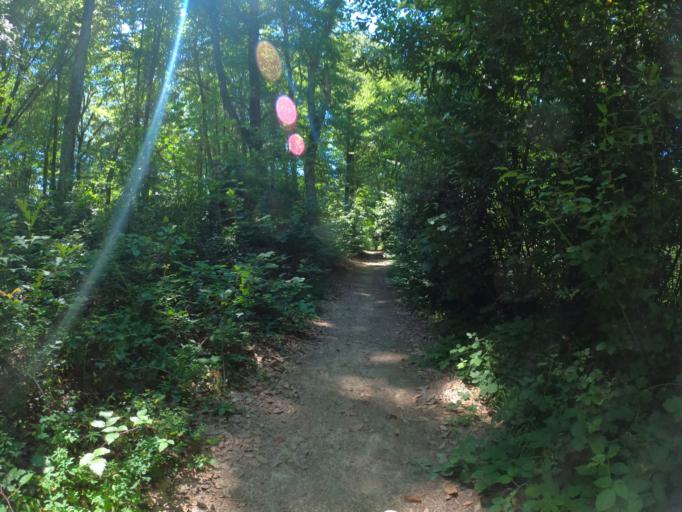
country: FR
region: Aquitaine
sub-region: Departement des Pyrenees-Atlantiques
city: Boucau
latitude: 43.5284
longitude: -1.4520
